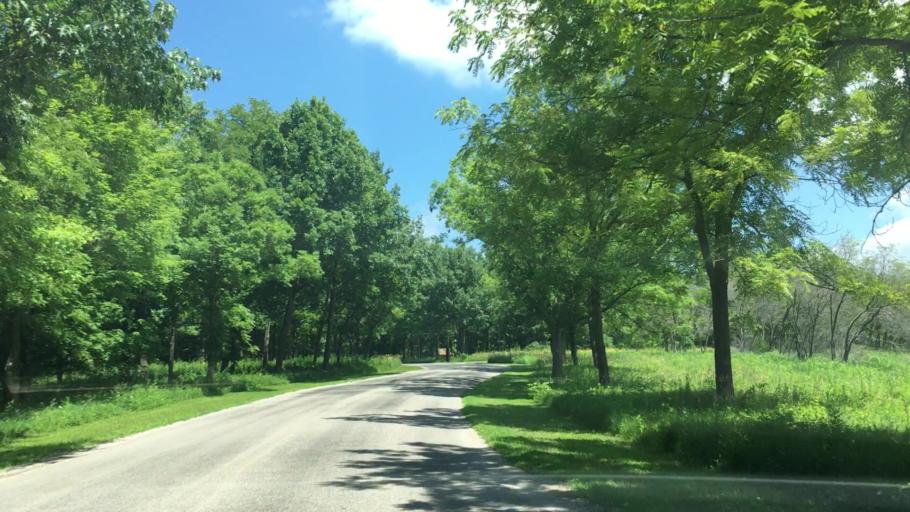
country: US
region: Iowa
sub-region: Johnson County
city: Tiffin
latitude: 41.7241
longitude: -91.7247
